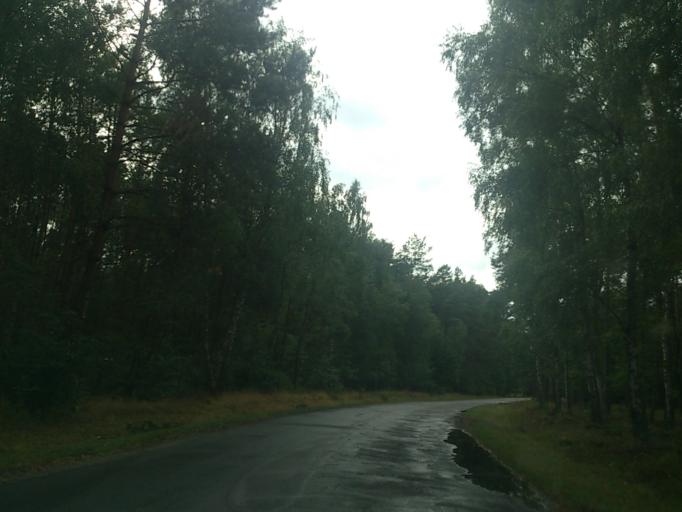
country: PL
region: Greater Poland Voivodeship
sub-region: Powiat gnieznienski
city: Kiszkowo
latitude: 52.5205
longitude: 17.1714
